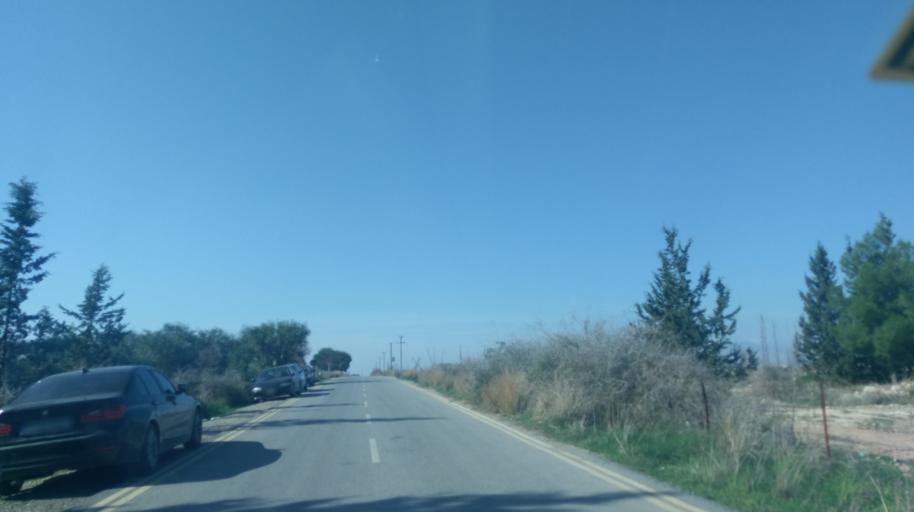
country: CY
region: Lefkosia
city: Geri
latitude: 35.1604
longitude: 33.5012
